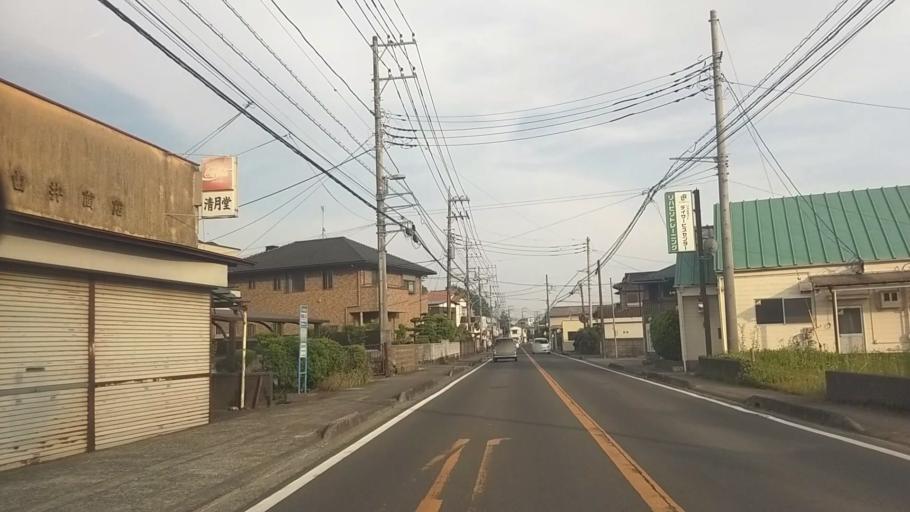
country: JP
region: Kanagawa
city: Odawara
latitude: 35.3098
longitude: 139.1212
